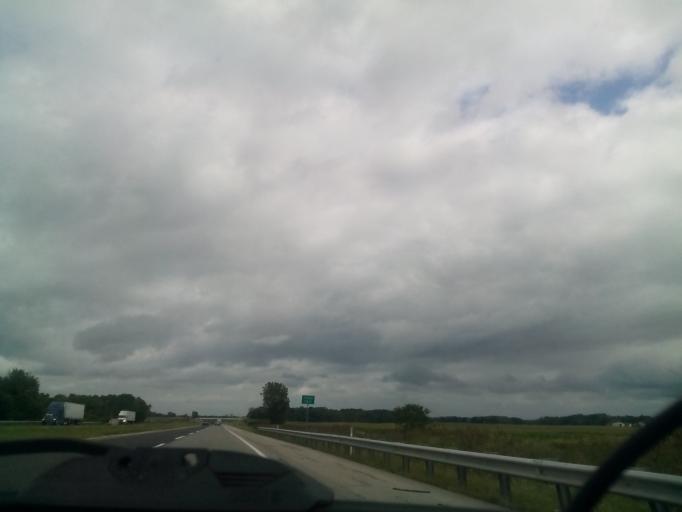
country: US
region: Indiana
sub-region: Steuben County
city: Fremont
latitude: 41.6909
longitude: -84.8989
